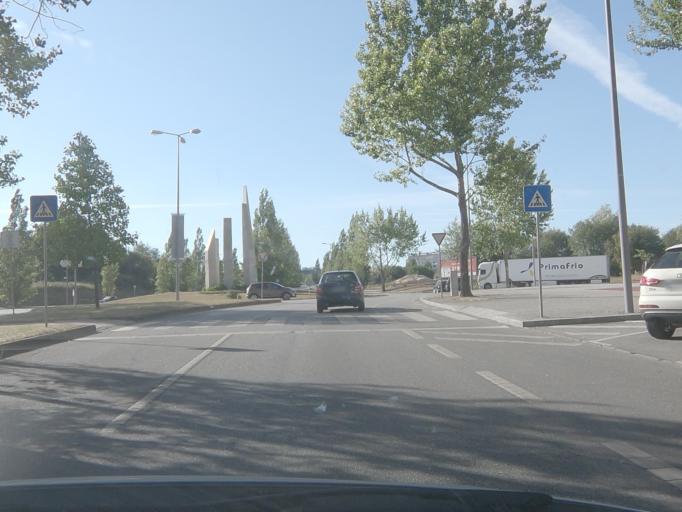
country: PT
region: Viseu
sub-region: Viseu
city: Viseu
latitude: 40.6677
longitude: -7.9179
